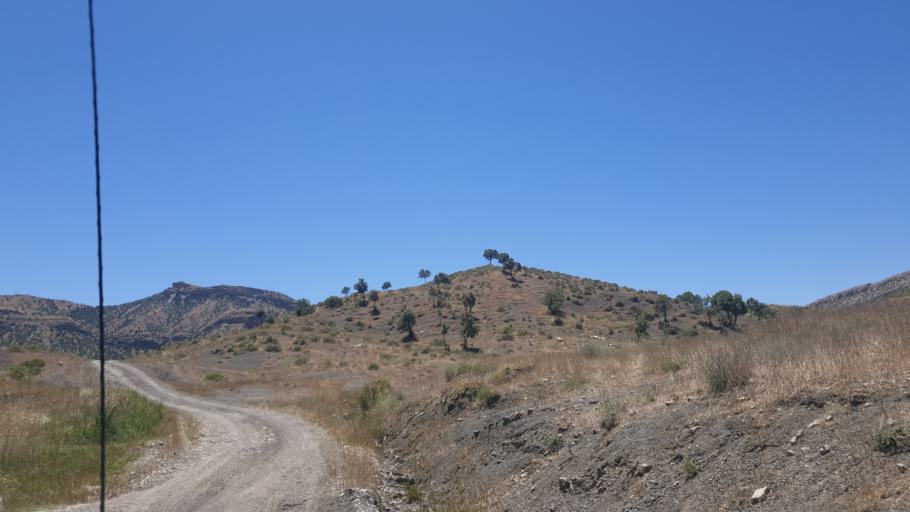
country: IQ
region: Arbil
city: Nahiyat Hiran
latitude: 36.2014
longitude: 44.4230
